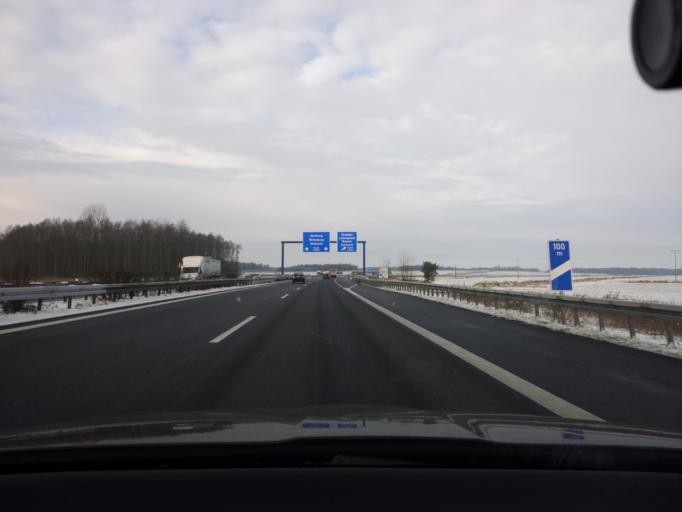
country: DE
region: Mecklenburg-Vorpommern
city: Neustadt-Glewe
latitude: 53.4196
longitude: 11.5331
